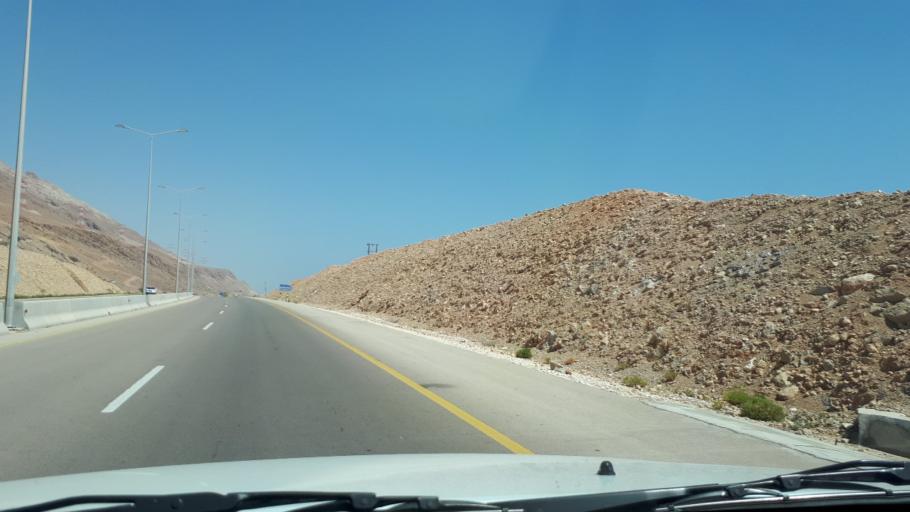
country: OM
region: Ash Sharqiyah
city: Sur
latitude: 22.7828
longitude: 59.2797
